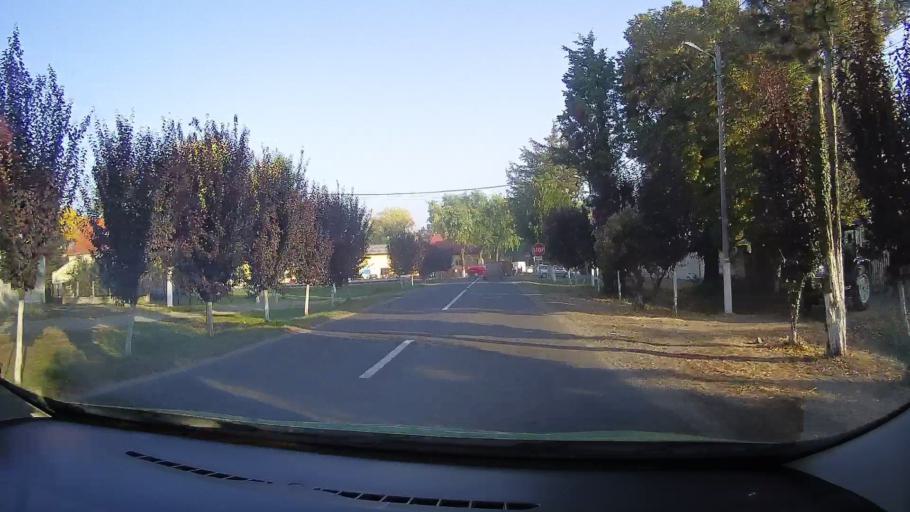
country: RO
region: Arad
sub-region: Comuna Curtici
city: Curtici
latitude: 46.3384
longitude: 21.3081
